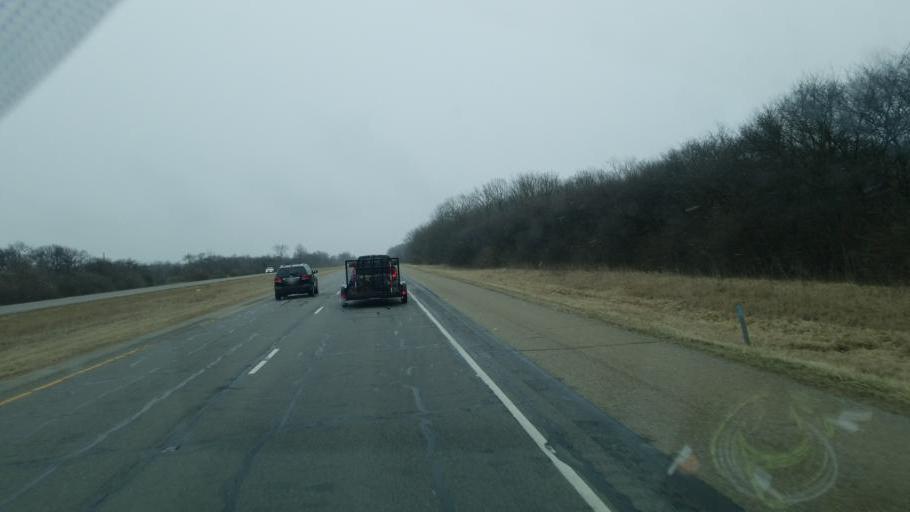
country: US
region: Indiana
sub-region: Miami County
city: Peru
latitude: 40.8076
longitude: -86.0139
